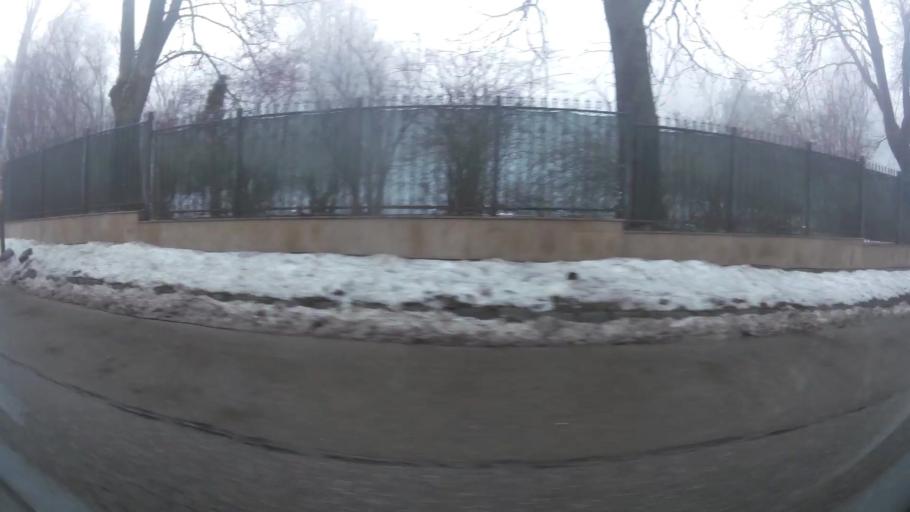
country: BG
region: Sofia-Capital
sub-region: Stolichna Obshtina
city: Sofia
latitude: 42.6546
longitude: 23.2498
